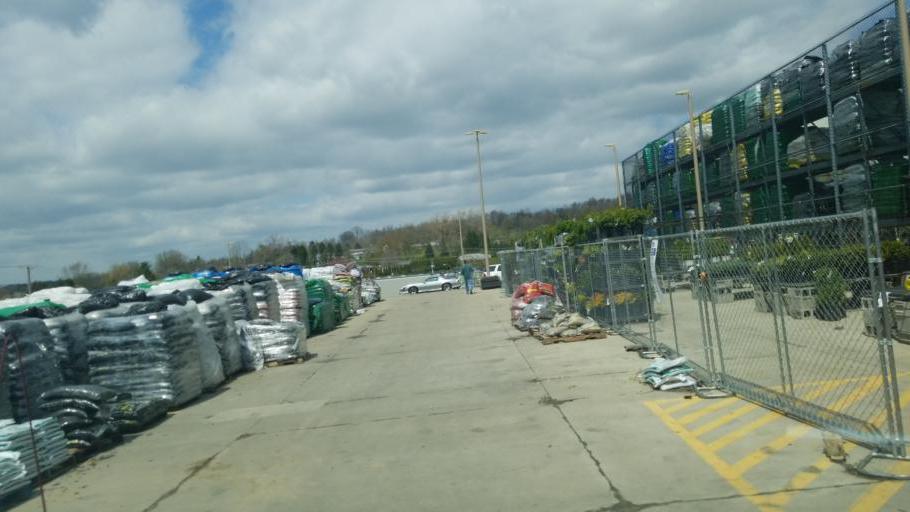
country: US
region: Ohio
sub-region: Knox County
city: Mount Vernon
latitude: 40.3989
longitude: -82.4524
